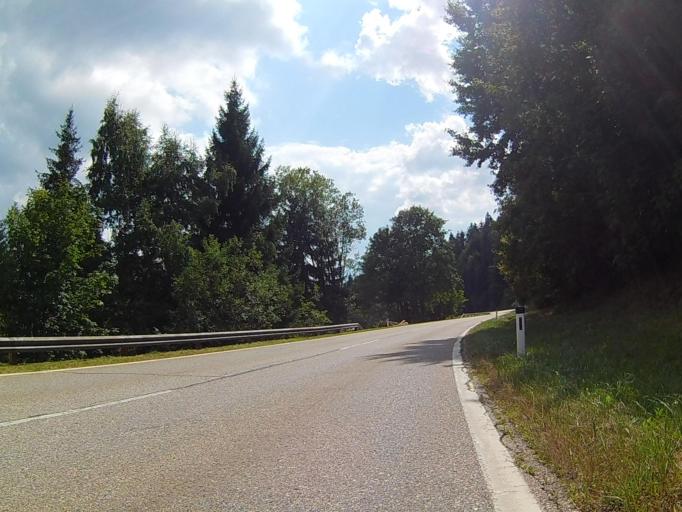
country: AT
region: Styria
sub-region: Politischer Bezirk Deutschlandsberg
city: Soboth
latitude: 46.6914
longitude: 15.1023
